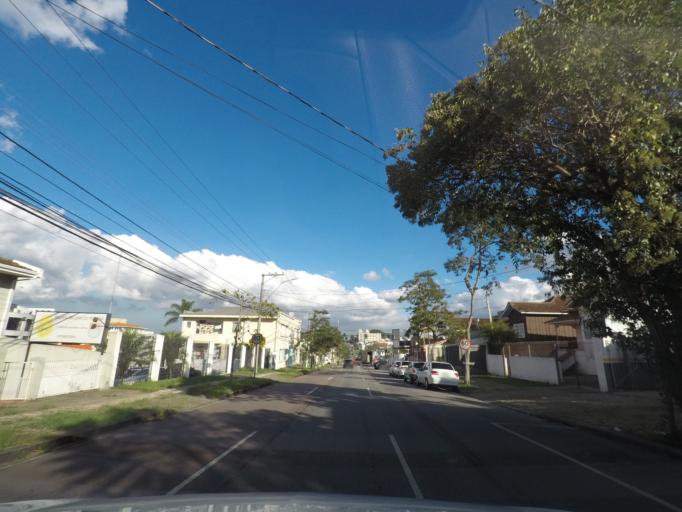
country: BR
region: Parana
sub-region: Curitiba
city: Curitiba
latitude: -25.4550
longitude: -49.2625
